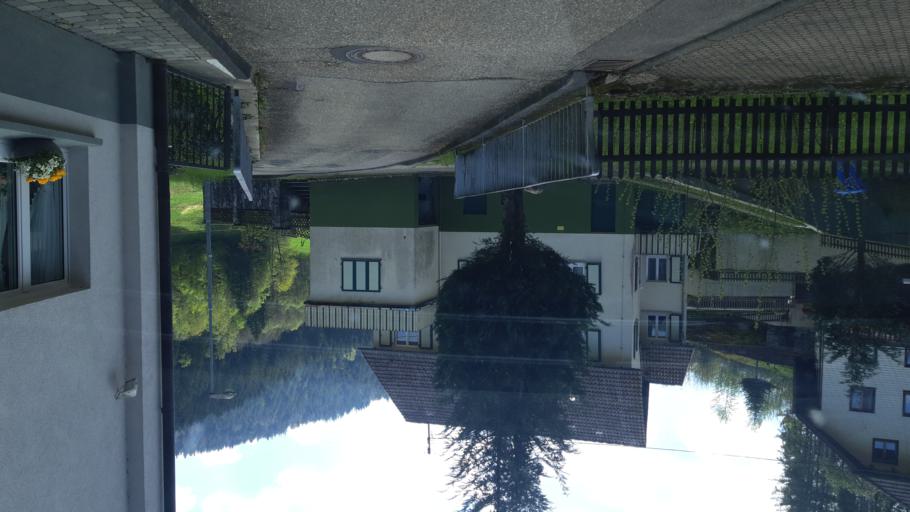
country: DE
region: Baden-Wuerttemberg
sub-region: Freiburg Region
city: Gutenbach
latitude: 48.0866
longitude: 8.0850
